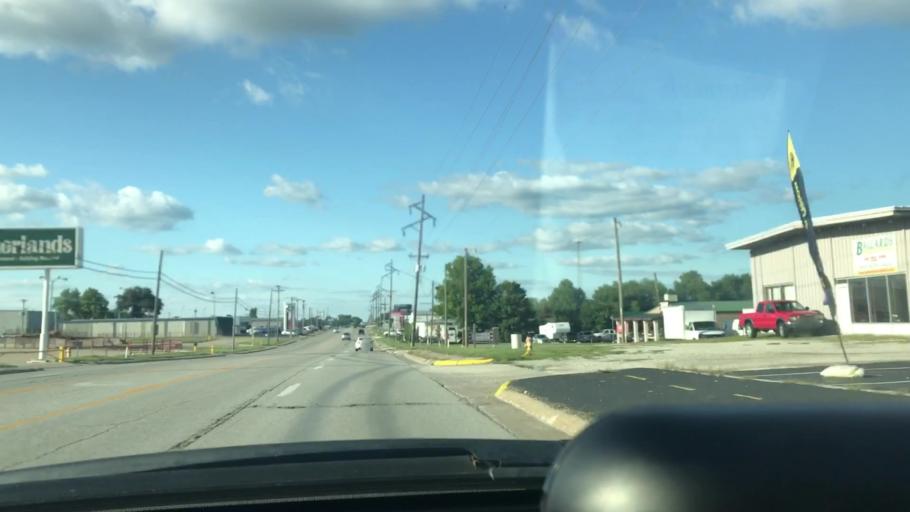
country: US
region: Missouri
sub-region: Pettis County
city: Sedalia
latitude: 38.6774
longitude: -93.2515
